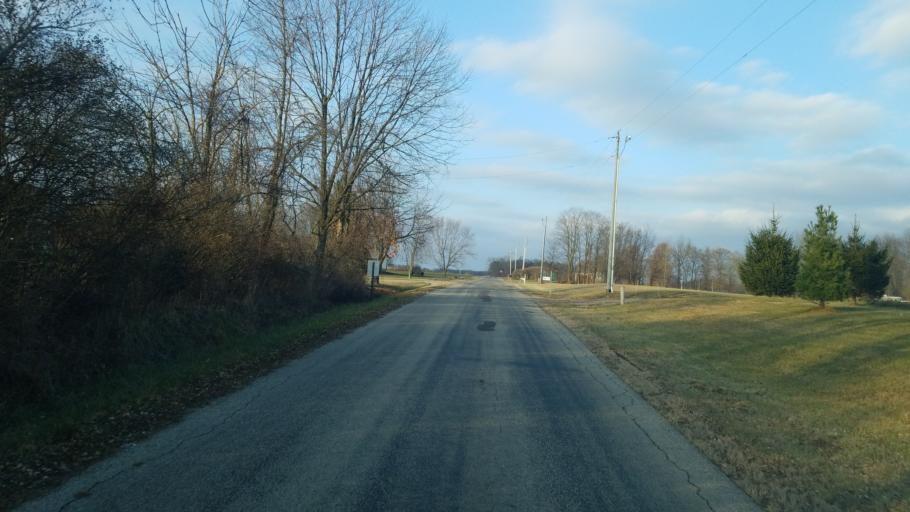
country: US
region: Ohio
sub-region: Knox County
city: Centerburg
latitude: 40.3147
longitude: -82.6358
